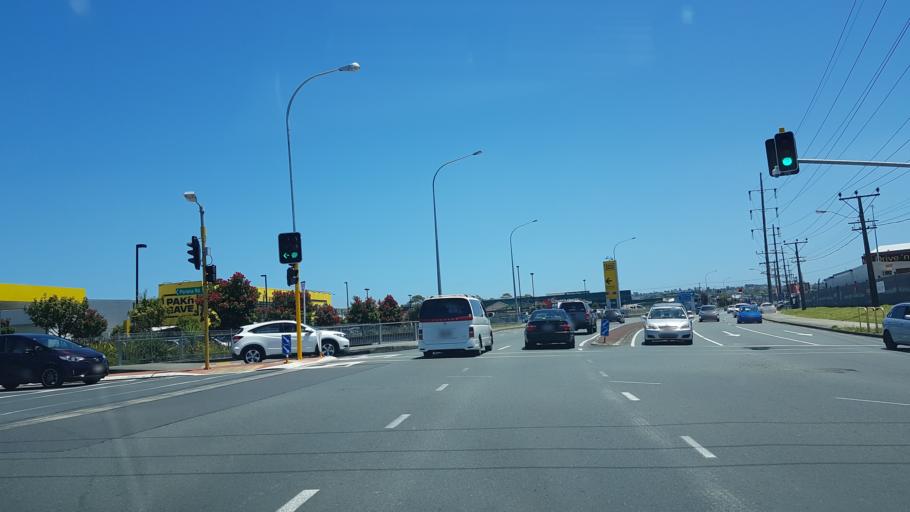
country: NZ
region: Auckland
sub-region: Auckland
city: North Shore
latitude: -36.7794
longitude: 174.7459
